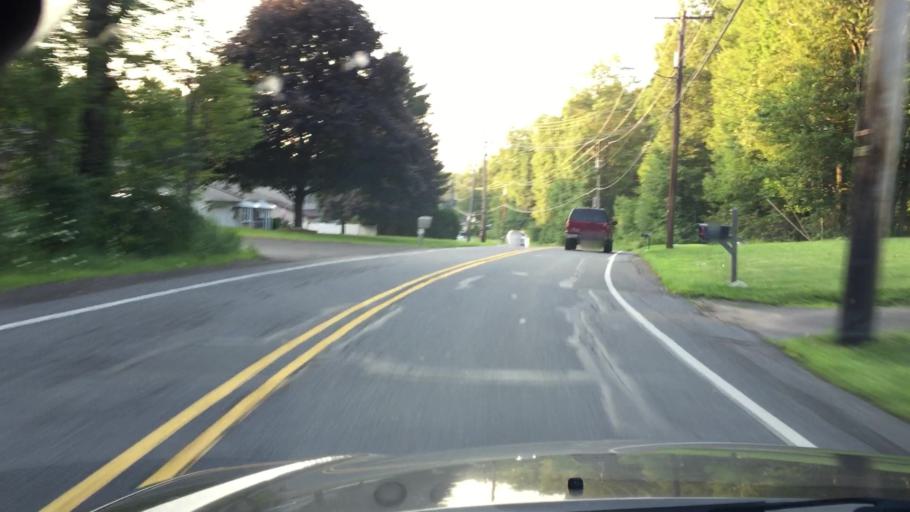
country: US
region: Pennsylvania
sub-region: Luzerne County
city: Harleigh
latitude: 40.9845
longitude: -75.9755
